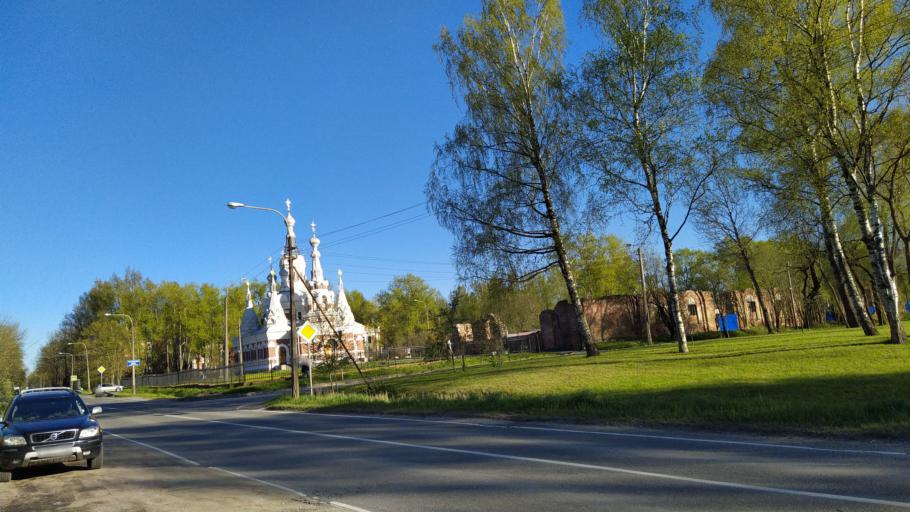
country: RU
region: St.-Petersburg
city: Pavlovsk
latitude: 59.6791
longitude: 30.4489
